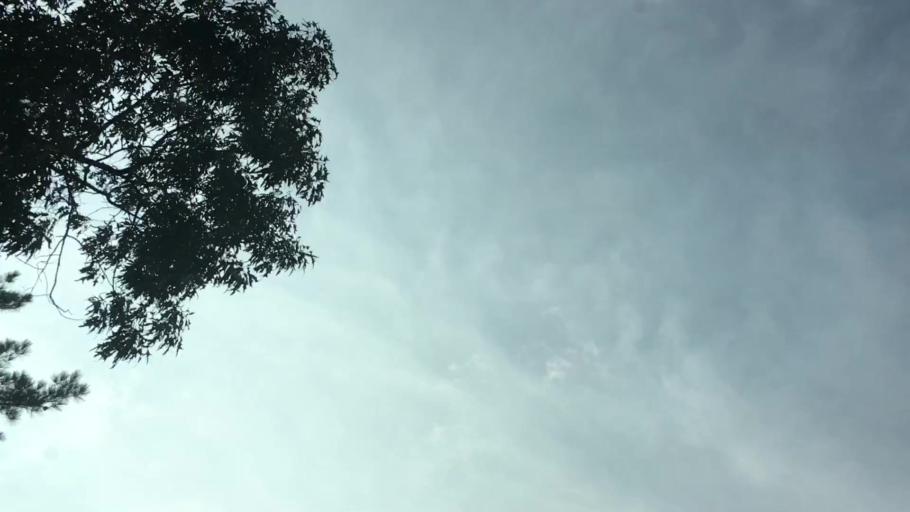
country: US
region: Alabama
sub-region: Bibb County
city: Woodstock
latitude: 33.2171
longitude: -87.1045
